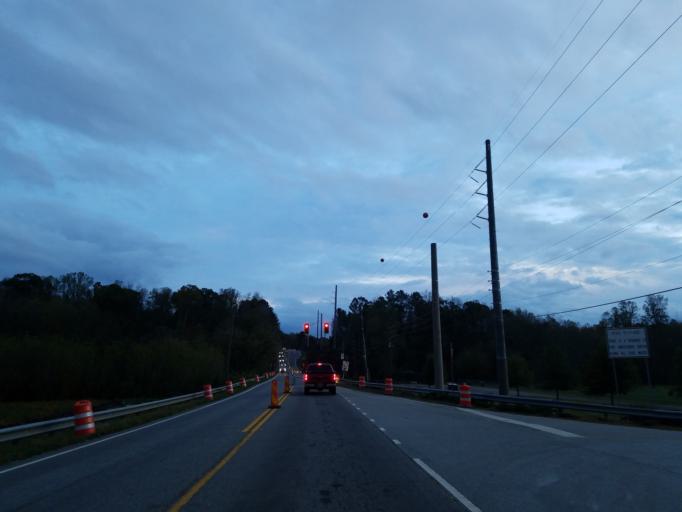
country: US
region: Georgia
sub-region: Dawson County
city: Dawsonville
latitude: 34.3593
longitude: -84.1136
